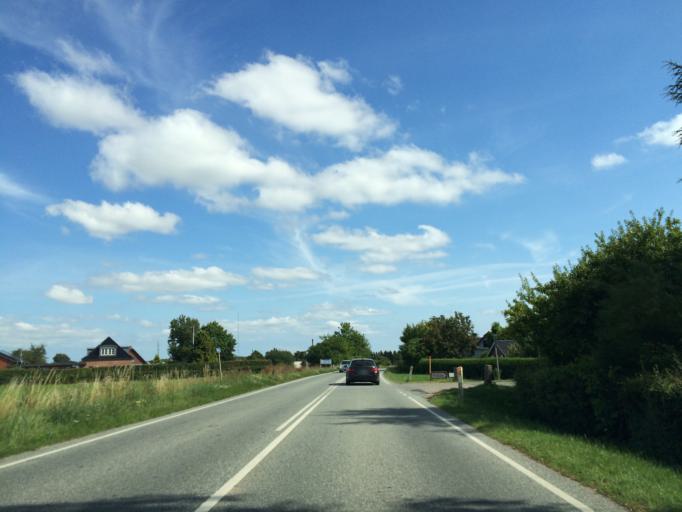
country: DK
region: Central Jutland
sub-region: Syddjurs Kommune
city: Ronde
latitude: 56.3104
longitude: 10.4410
